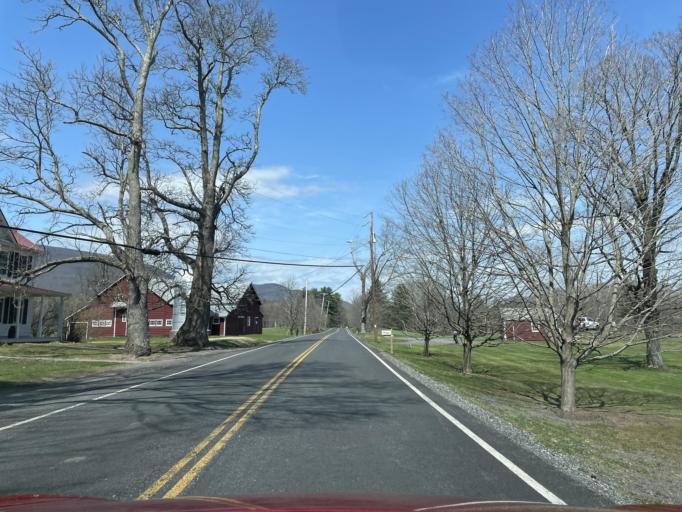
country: US
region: New York
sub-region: Ulster County
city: Manorville
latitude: 42.1234
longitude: -74.0212
